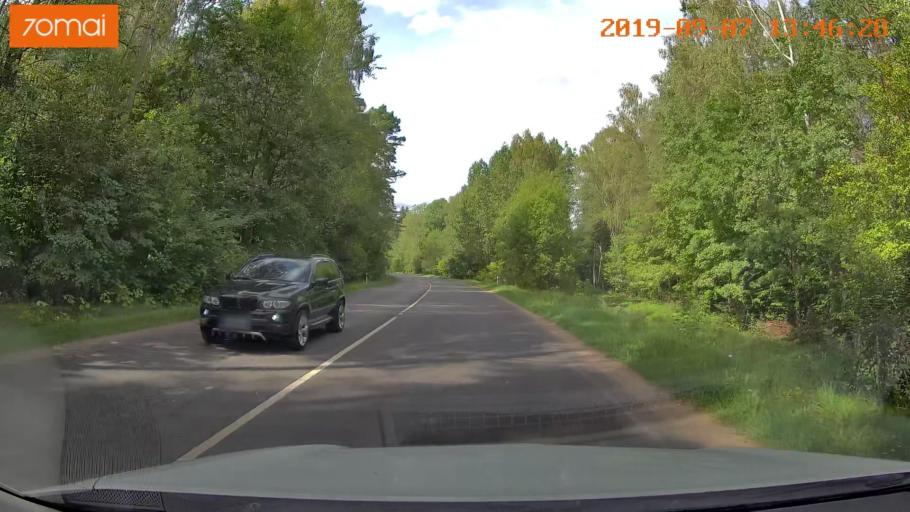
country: LT
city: Baltoji Voke
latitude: 54.5912
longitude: 25.2323
